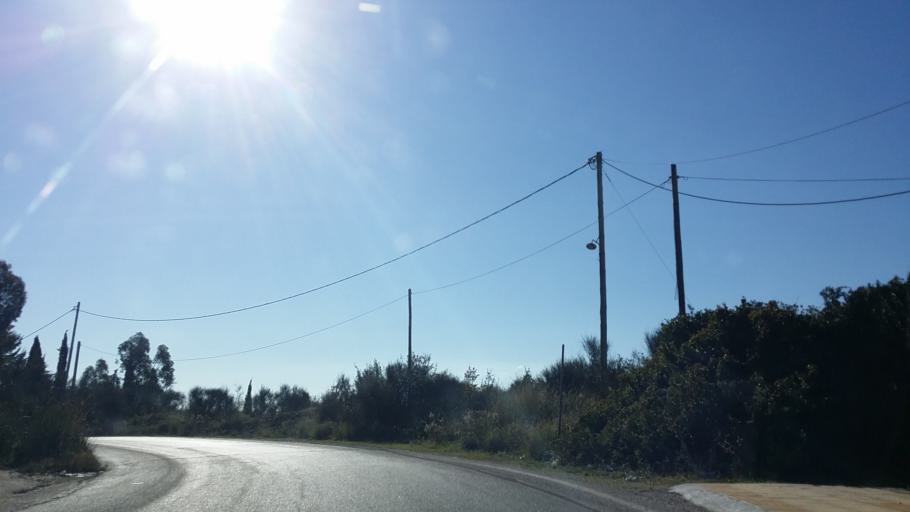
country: GR
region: West Greece
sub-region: Nomos Aitolias kai Akarnanias
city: Palairos
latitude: 38.7685
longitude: 20.8811
